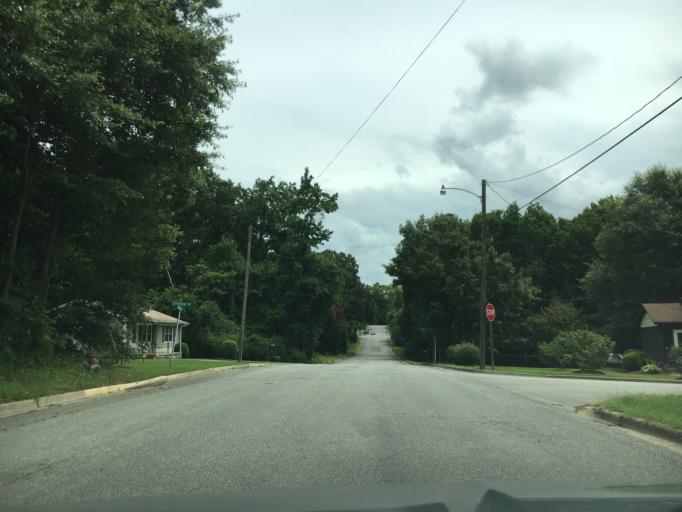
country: US
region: Virginia
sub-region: Halifax County
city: South Boston
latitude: 36.7082
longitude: -78.9029
